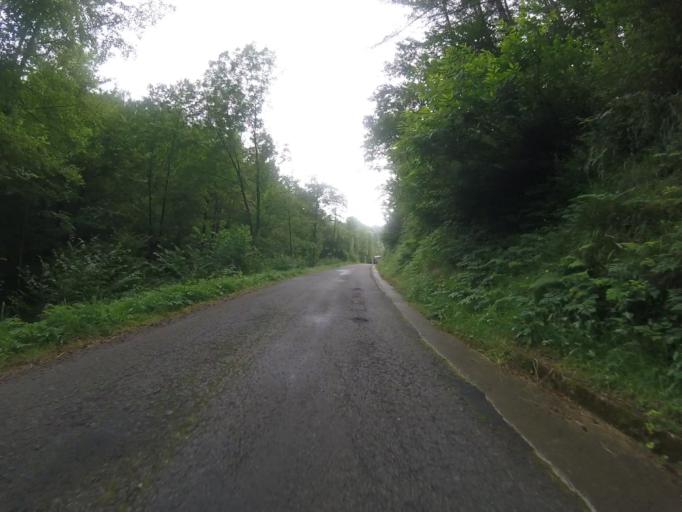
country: ES
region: Navarre
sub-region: Provincia de Navarra
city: Leitza
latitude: 43.0848
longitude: -1.8973
